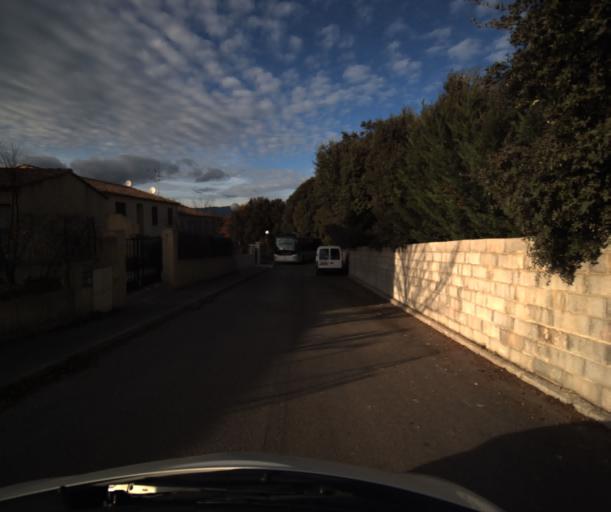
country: FR
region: Provence-Alpes-Cote d'Azur
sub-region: Departement du Vaucluse
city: Pertuis
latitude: 43.6952
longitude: 5.5294
